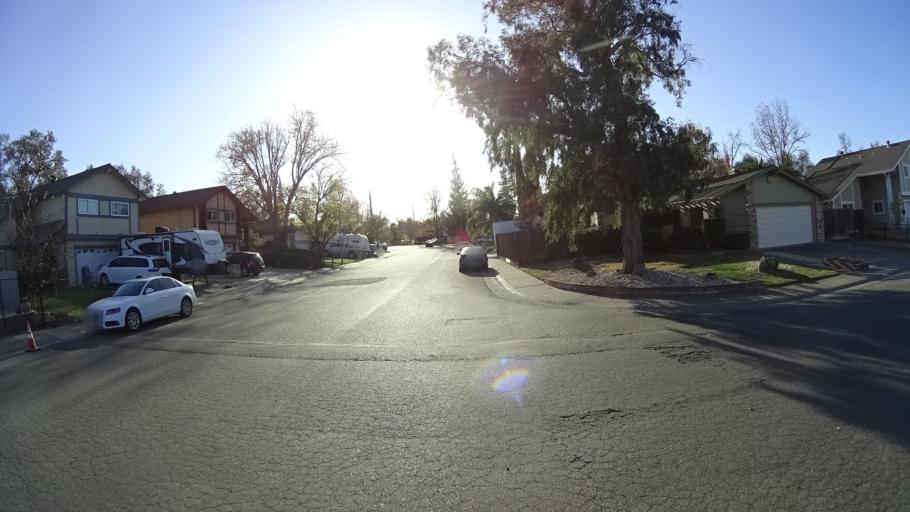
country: US
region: California
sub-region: Sacramento County
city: Citrus Heights
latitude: 38.7010
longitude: -121.3054
